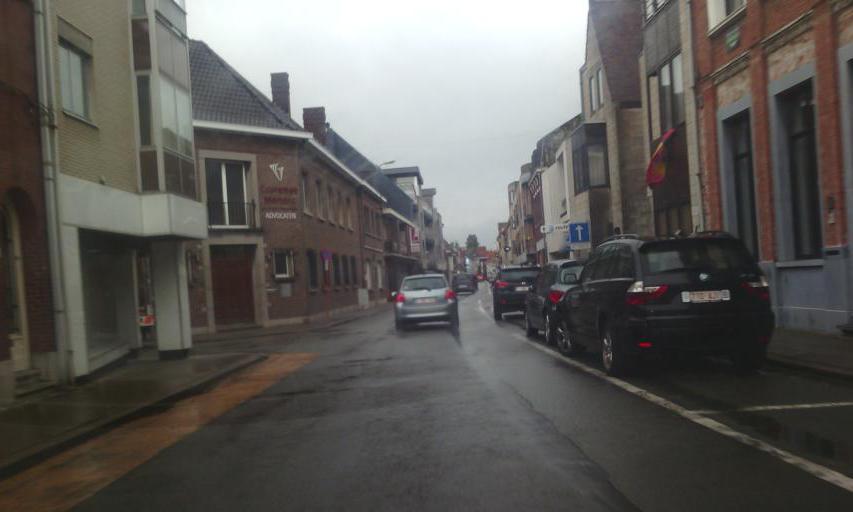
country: BE
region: Flanders
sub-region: Provincie Oost-Vlaanderen
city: Zele
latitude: 51.0661
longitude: 4.0303
